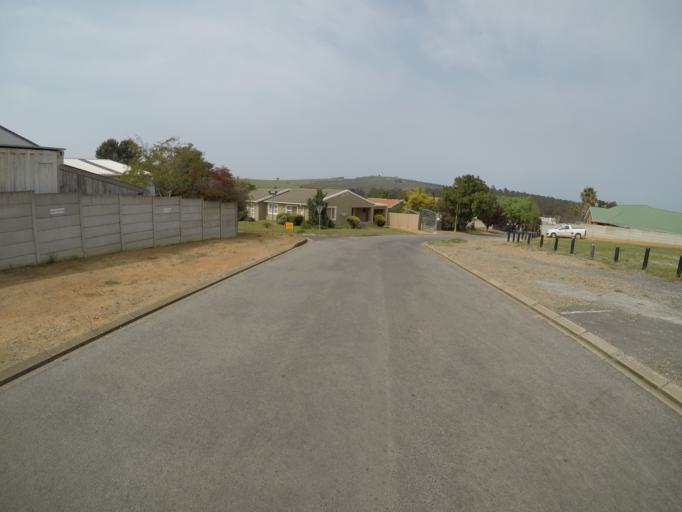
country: ZA
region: Western Cape
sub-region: West Coast District Municipality
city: Malmesbury
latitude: -33.4602
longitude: 18.7416
